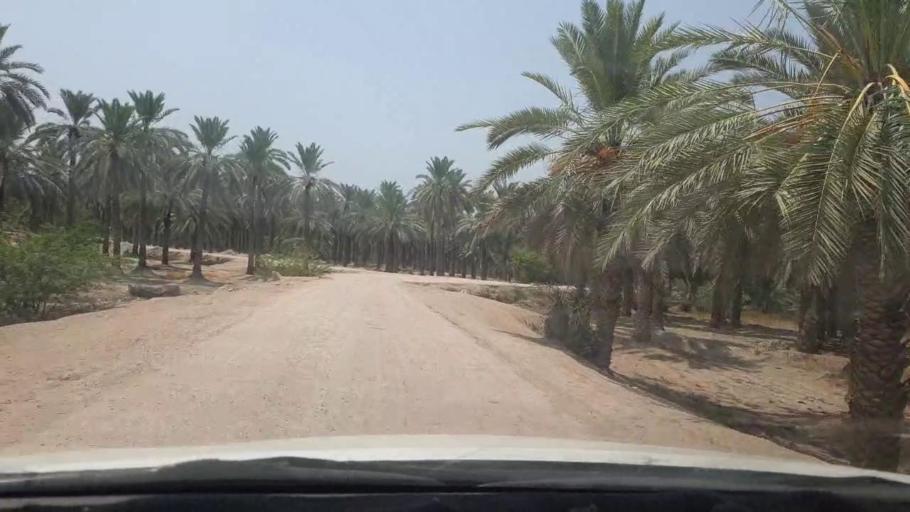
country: PK
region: Sindh
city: Khairpur
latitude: 27.4990
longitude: 68.8787
